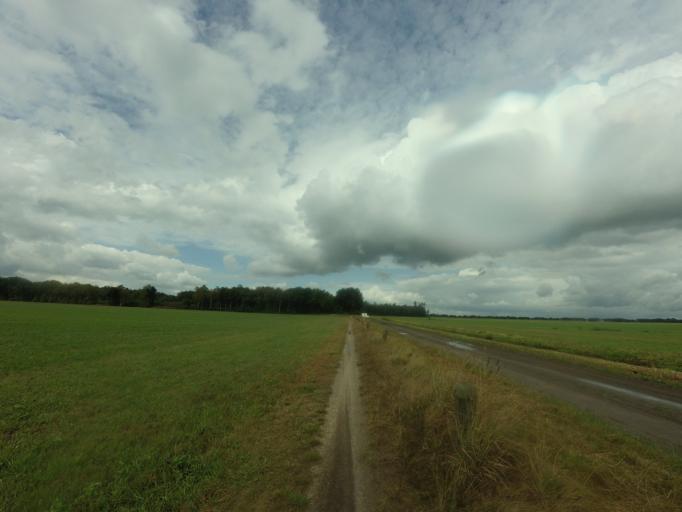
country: NL
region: Overijssel
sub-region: Gemeente Dalfsen
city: Dalfsen
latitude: 52.6112
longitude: 6.3376
